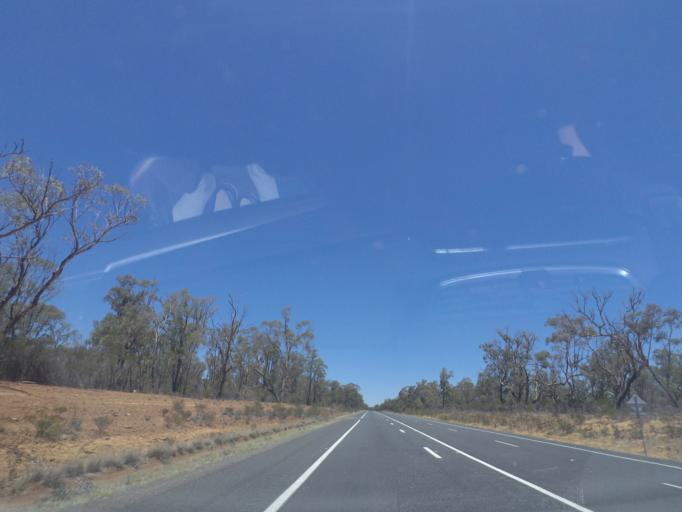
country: AU
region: New South Wales
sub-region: Warrumbungle Shire
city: Coonabarabran
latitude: -30.8726
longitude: 149.4496
